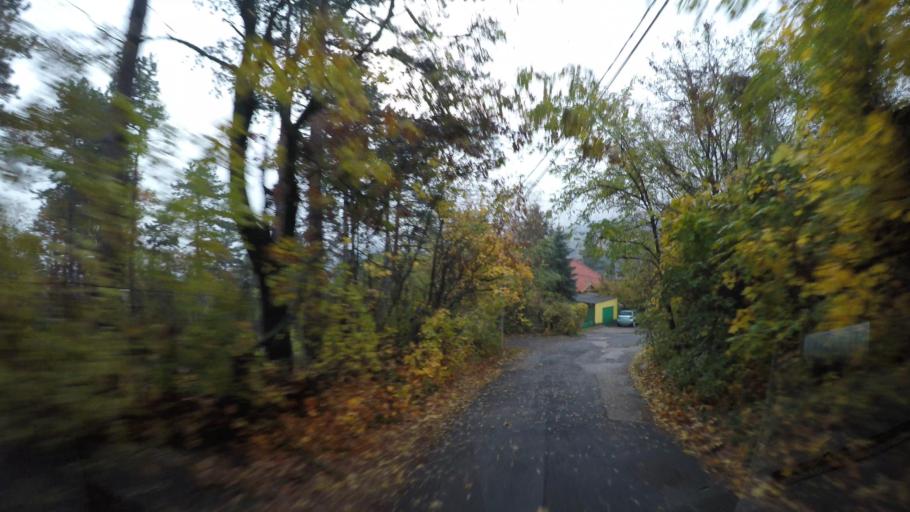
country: HU
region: Pest
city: Leanyfalu
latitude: 47.7208
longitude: 19.0841
